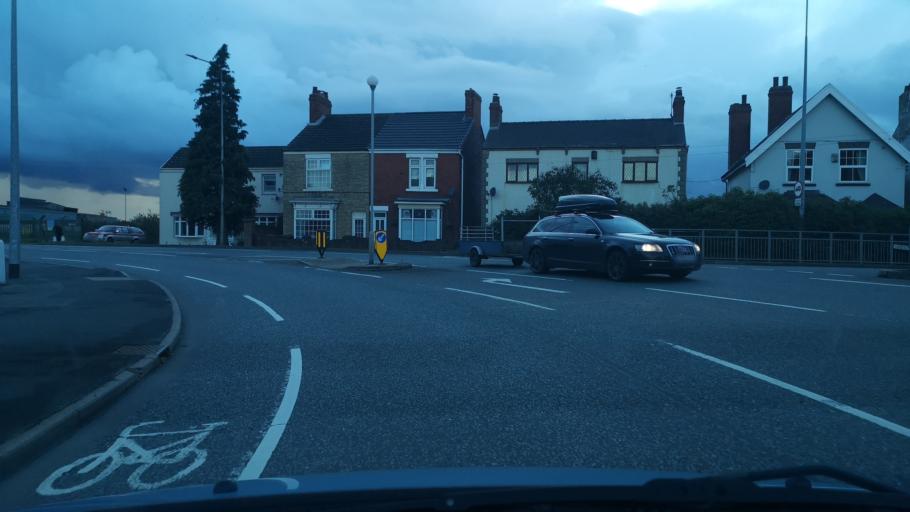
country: GB
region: England
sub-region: North Lincolnshire
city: Gunness
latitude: 53.5905
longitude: -0.7279
